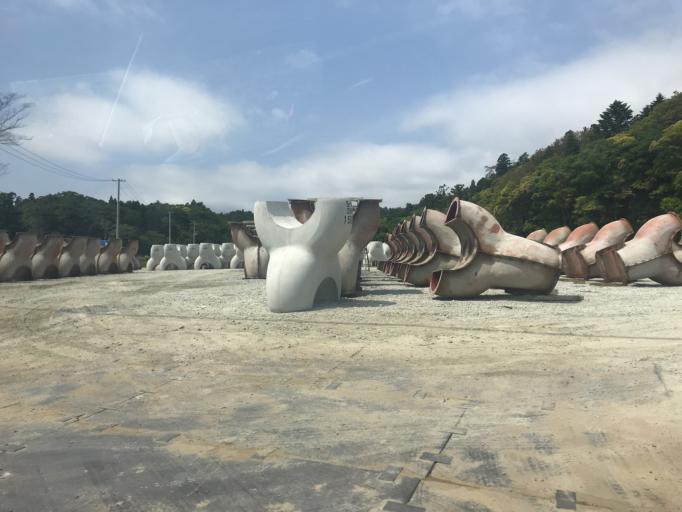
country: JP
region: Fukushima
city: Namie
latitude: 37.3073
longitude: 141.0211
